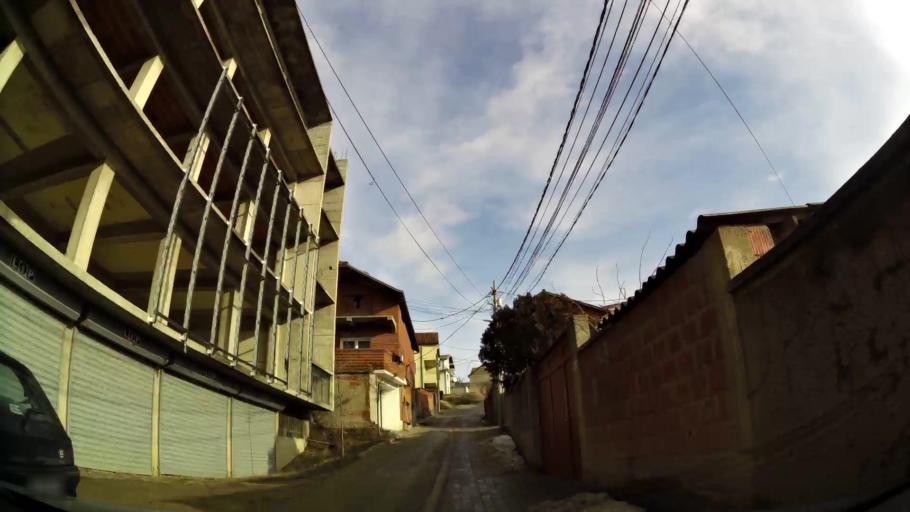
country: XK
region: Pristina
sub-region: Komuna e Prishtines
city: Pristina
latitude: 42.6708
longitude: 21.1776
